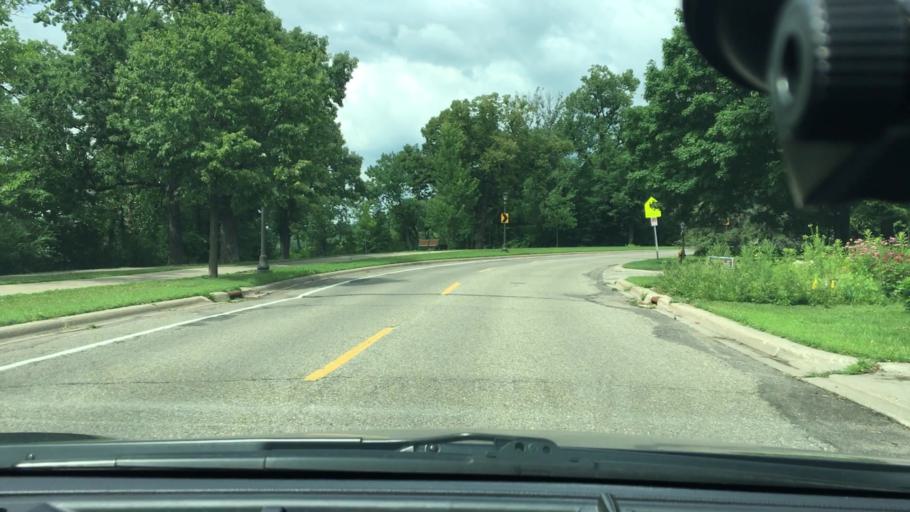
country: US
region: Minnesota
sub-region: Dakota County
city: Mendota Heights
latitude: 44.9207
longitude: -93.1989
